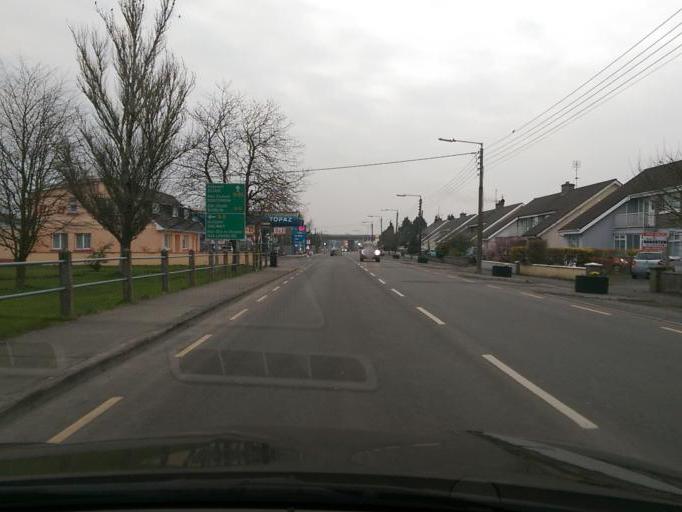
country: IE
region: Leinster
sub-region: An Iarmhi
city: Athlone
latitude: 53.4262
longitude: -7.9593
